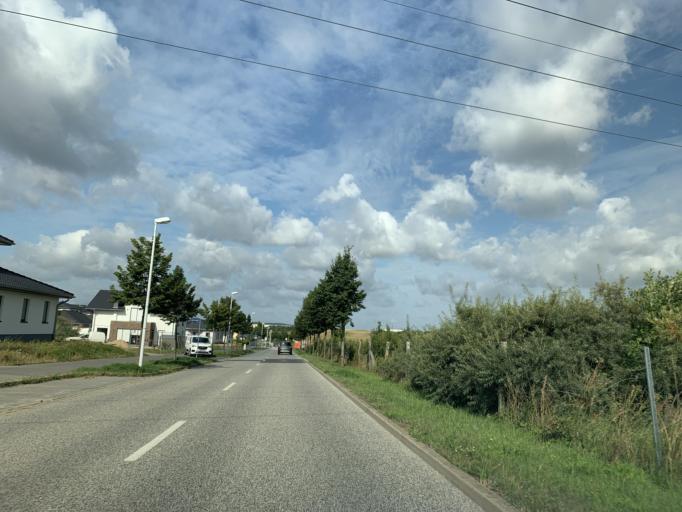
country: DE
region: Mecklenburg-Vorpommern
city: Neubrandenburg
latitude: 53.5284
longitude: 13.2805
